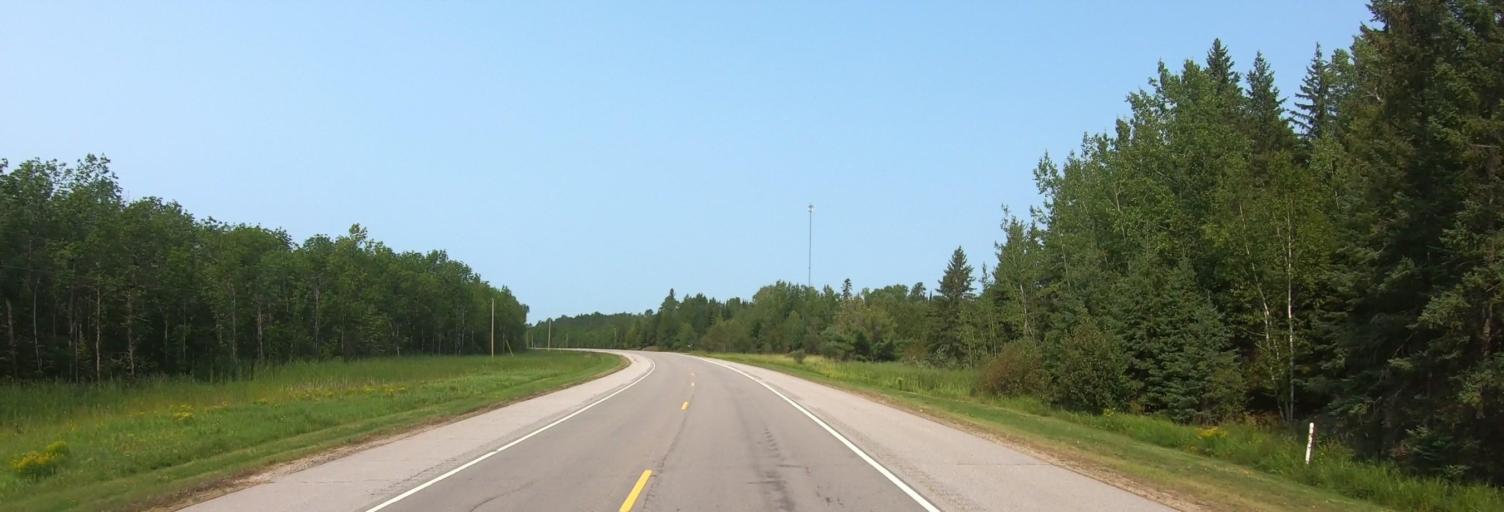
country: US
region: Minnesota
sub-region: Saint Louis County
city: Mountain Iron
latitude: 48.0915
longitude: -92.8276
